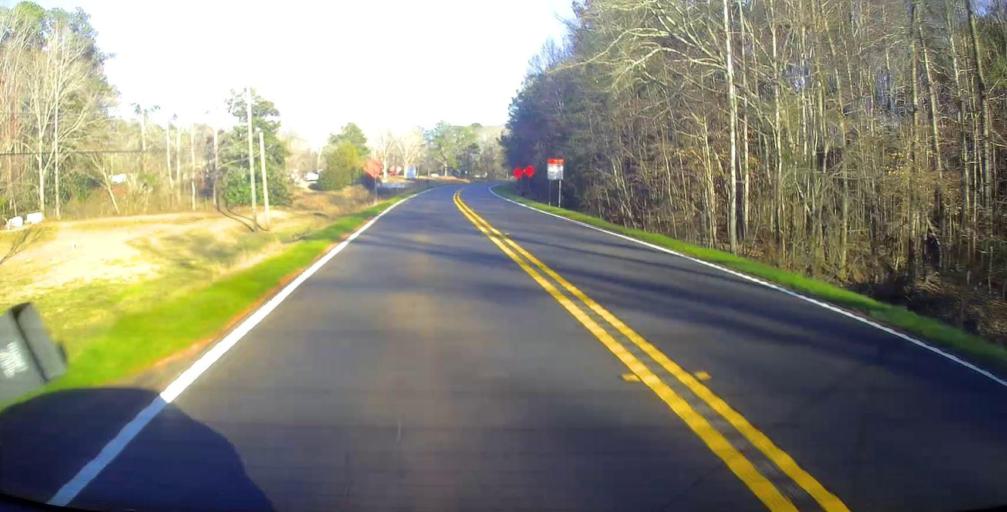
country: US
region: Georgia
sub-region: Meriwether County
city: Manchester
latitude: 32.8939
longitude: -84.7097
